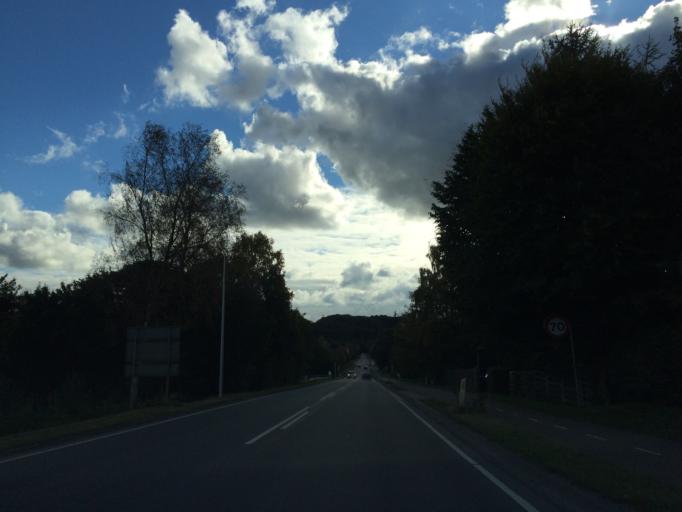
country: DK
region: Central Jutland
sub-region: Skanderborg Kommune
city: Ry
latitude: 56.1071
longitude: 9.7846
